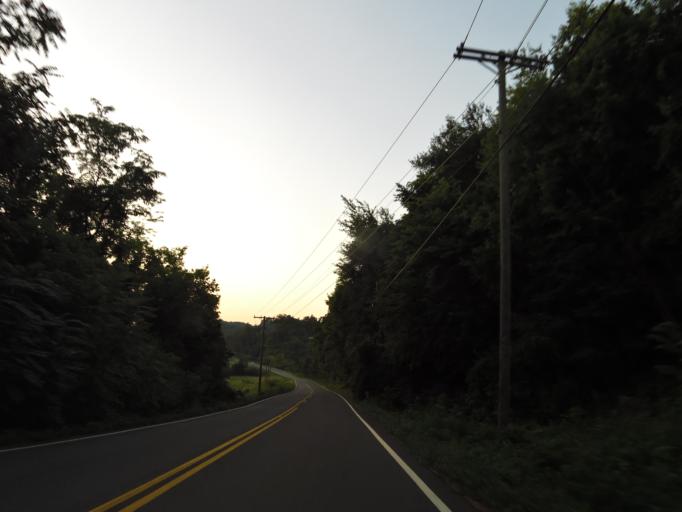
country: US
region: Tennessee
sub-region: Loudon County
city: Greenback
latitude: 35.5469
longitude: -84.0880
